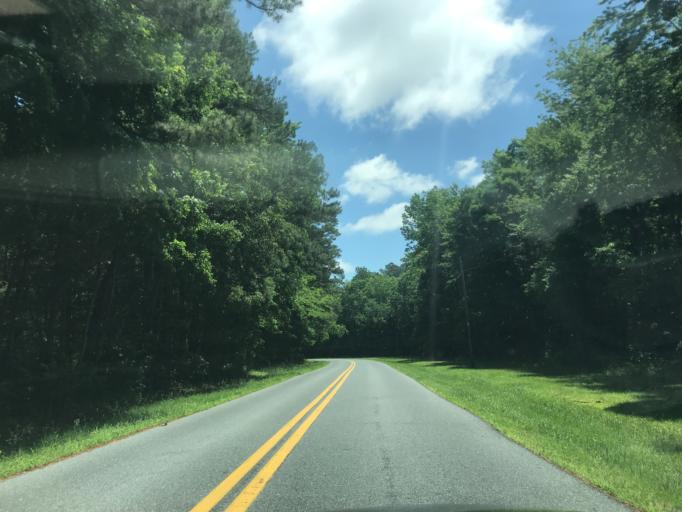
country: US
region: Maryland
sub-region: Caroline County
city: Federalsburg
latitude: 38.7405
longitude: -75.7095
